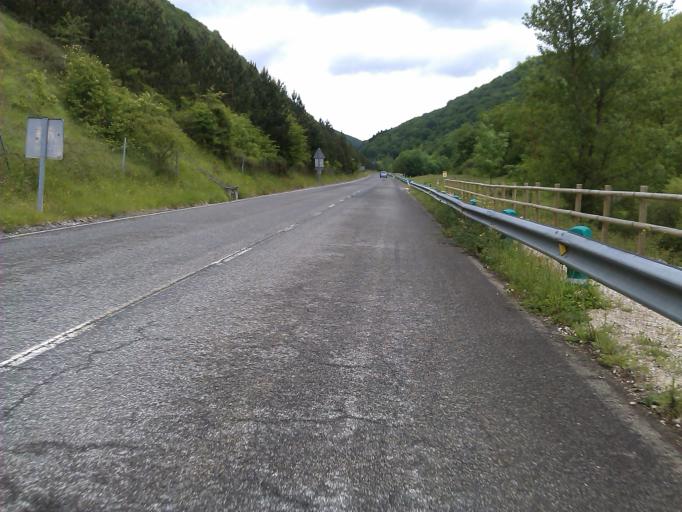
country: ES
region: Navarre
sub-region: Provincia de Navarra
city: Irurtzun
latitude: 42.9705
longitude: -1.8438
